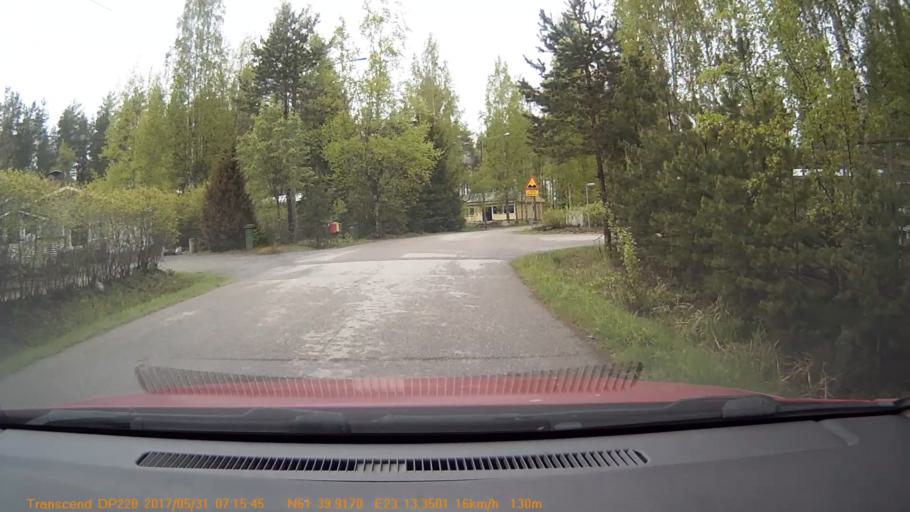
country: FI
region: Pirkanmaa
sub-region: Tampere
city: Haemeenkyroe
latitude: 61.6653
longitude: 23.2225
